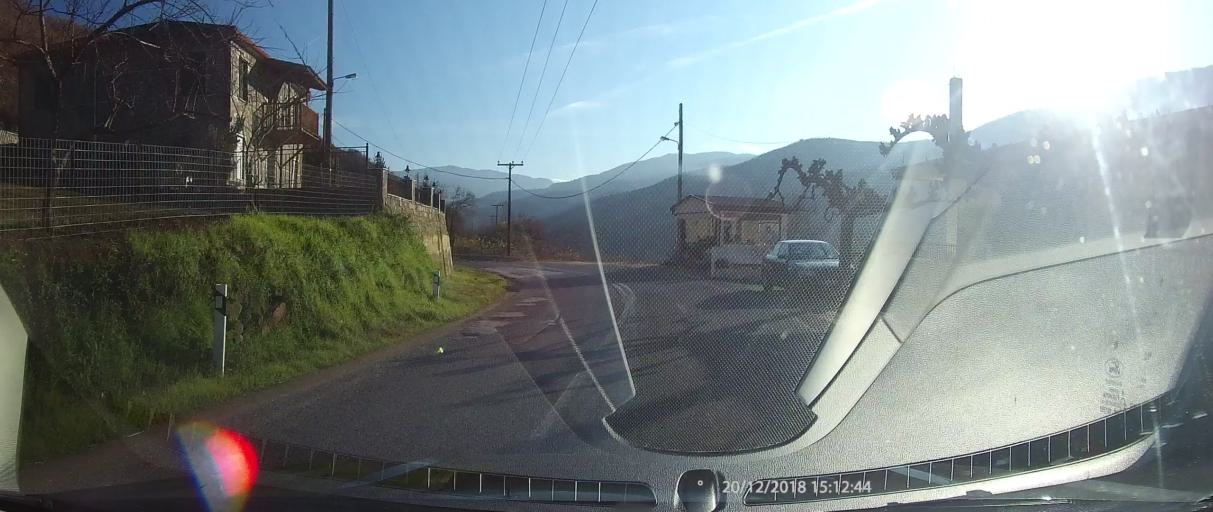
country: GR
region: Central Greece
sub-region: Nomos Fthiotidos
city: Makrakomi
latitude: 38.9402
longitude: 21.9639
